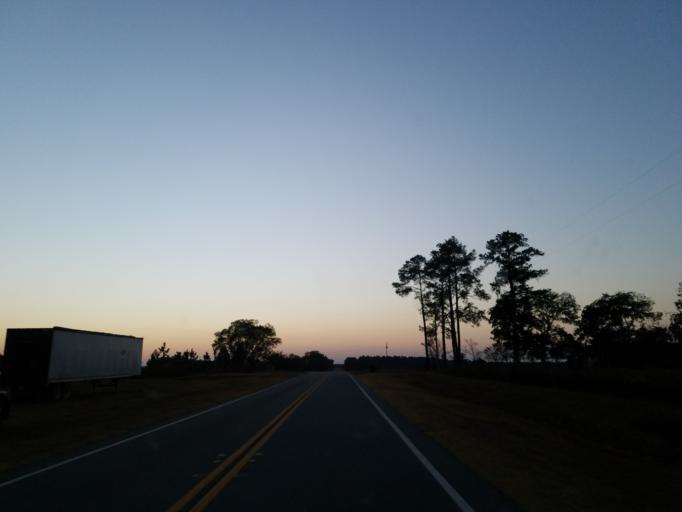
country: US
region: Georgia
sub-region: Wilcox County
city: Rochelle
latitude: 31.8159
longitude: -83.5182
